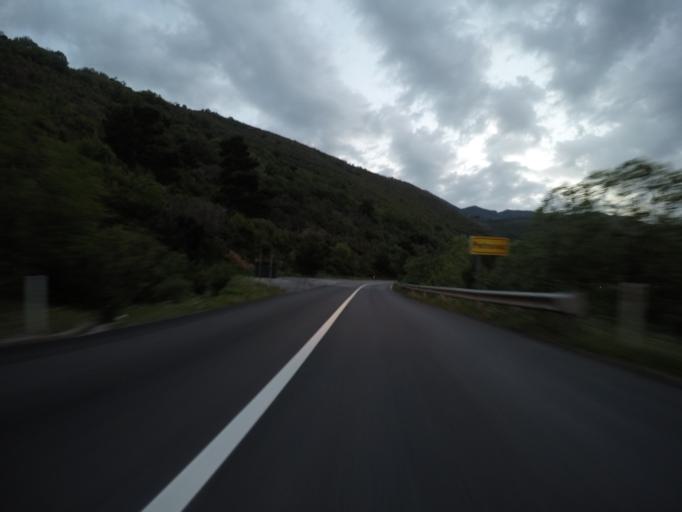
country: ME
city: Petrovac na Moru
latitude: 42.2092
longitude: 18.9328
